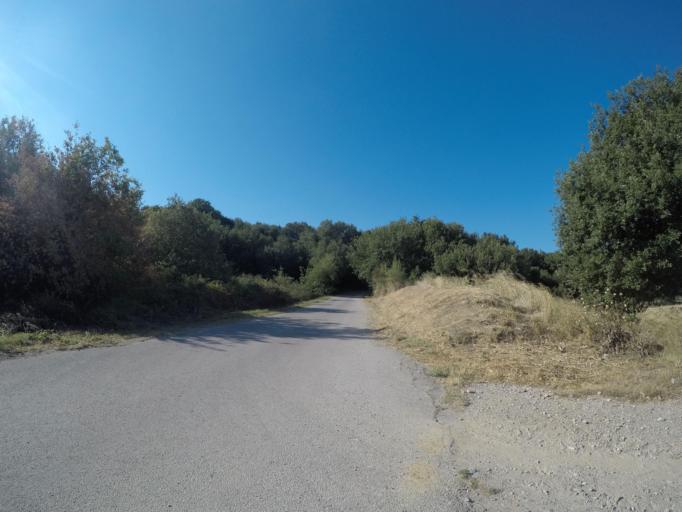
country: FR
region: Languedoc-Roussillon
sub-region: Departement des Pyrenees-Orientales
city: Pezilla-la-Riviere
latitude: 42.6821
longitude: 2.7656
